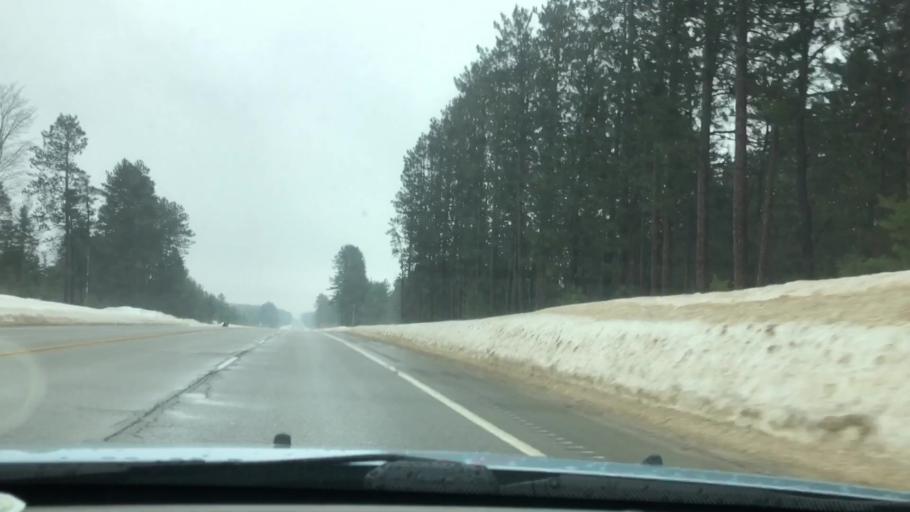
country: US
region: Michigan
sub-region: Otsego County
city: Gaylord
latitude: 45.0484
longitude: -84.7759
